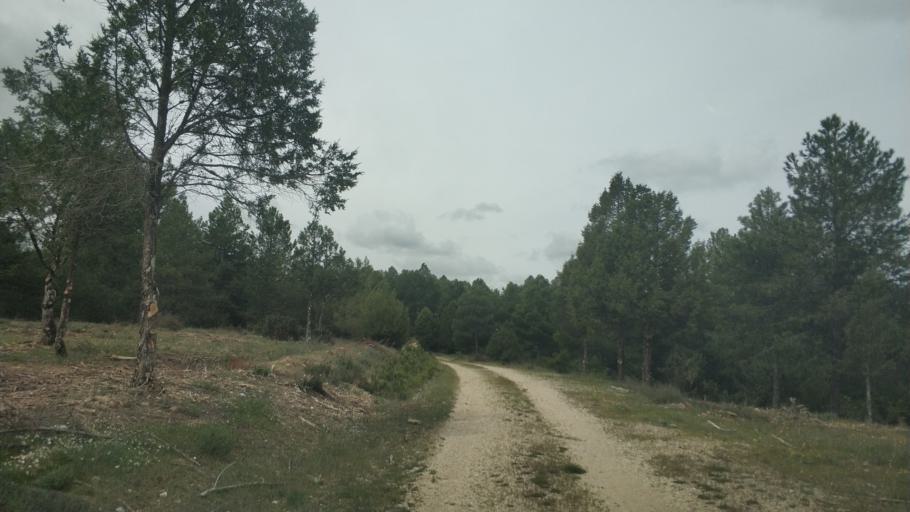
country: ES
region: Castille and Leon
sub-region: Provincia de Soria
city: Casarejos
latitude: 41.7645
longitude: -3.0613
